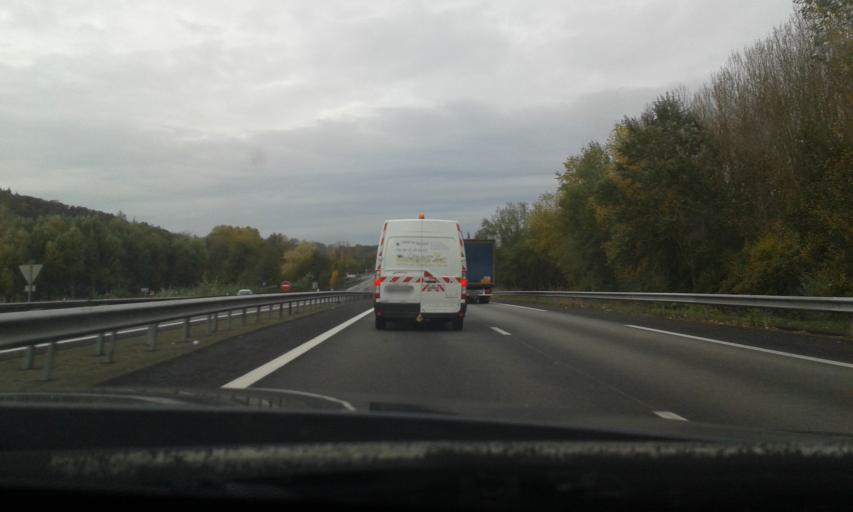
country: FR
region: Haute-Normandie
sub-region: Departement de l'Eure
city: Acquigny
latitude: 49.1852
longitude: 1.1702
